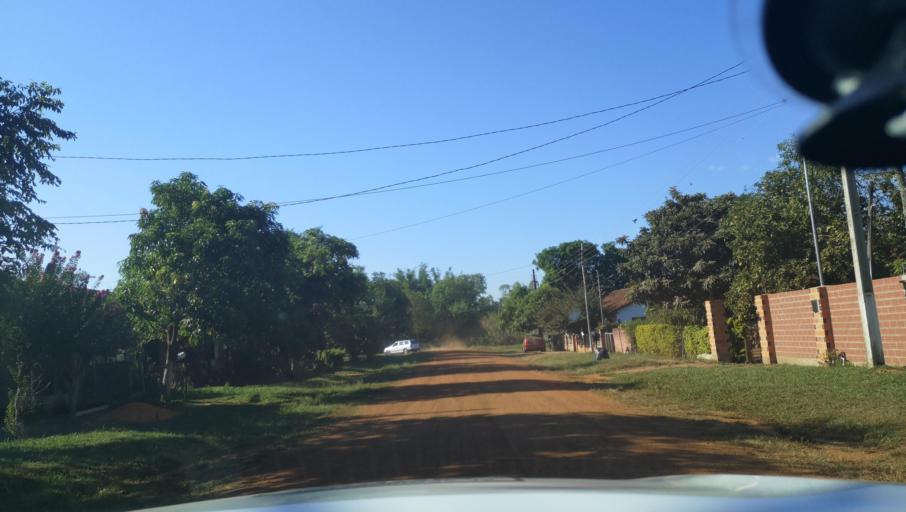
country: PY
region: Itapua
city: Carmen del Parana
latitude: -27.1714
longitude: -56.2405
